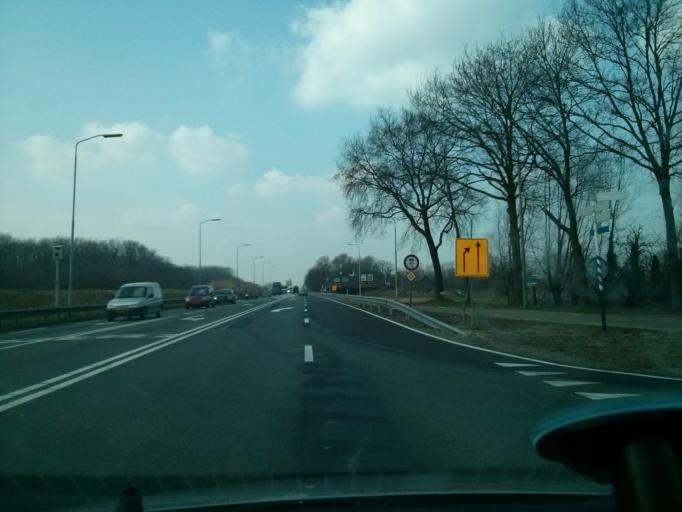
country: NL
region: North Brabant
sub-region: Gemeente Schijndel
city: Schijndel
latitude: 51.6448
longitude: 5.4609
